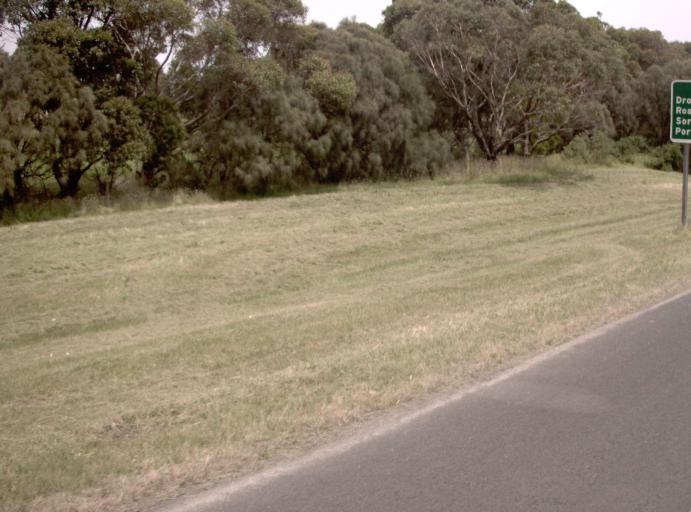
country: AU
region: Victoria
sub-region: Mornington Peninsula
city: Safety Beach
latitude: -38.3084
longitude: 145.0209
